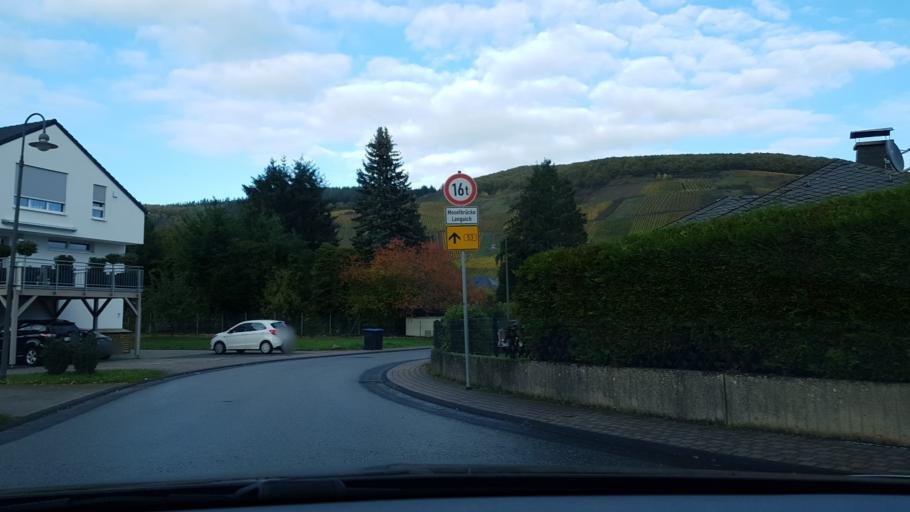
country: DE
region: Rheinland-Pfalz
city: Longuich
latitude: 49.8046
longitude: 6.7743
